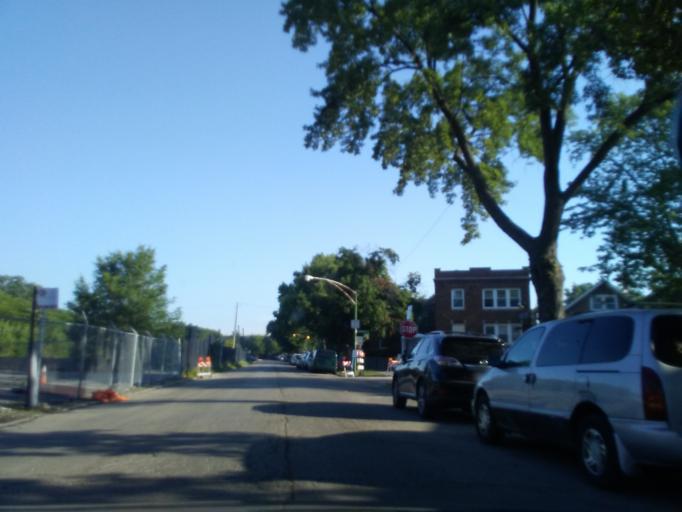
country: US
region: Illinois
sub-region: Cook County
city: Lincolnwood
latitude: 41.9342
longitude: -87.7320
